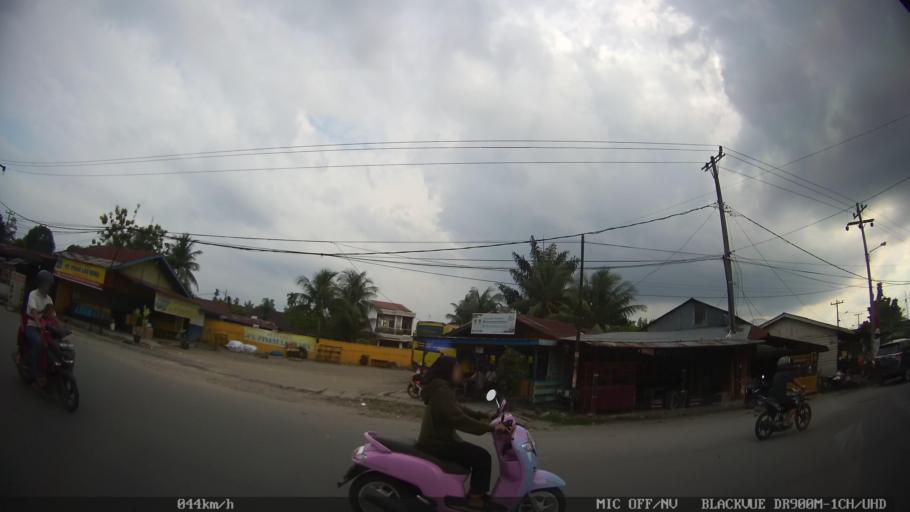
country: ID
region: North Sumatra
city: Medan
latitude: 3.5406
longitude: 98.6509
